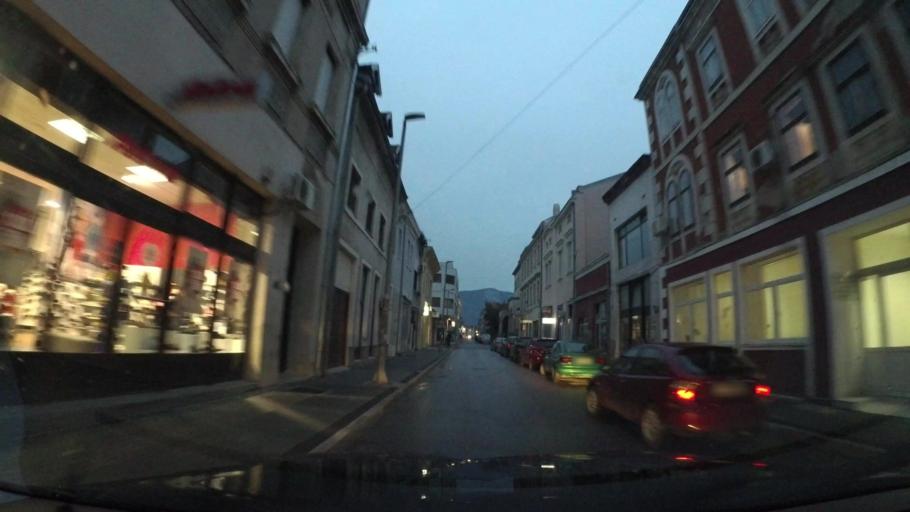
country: BA
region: Federation of Bosnia and Herzegovina
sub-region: Hercegovacko-Bosanski Kanton
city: Mostar
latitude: 43.3409
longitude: 17.8148
